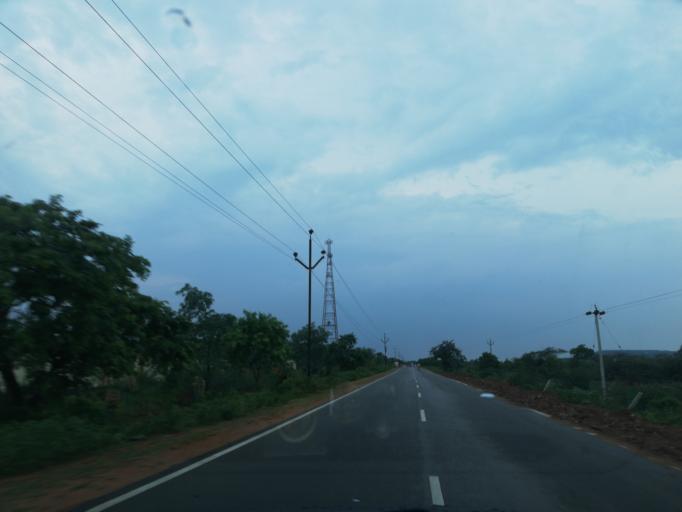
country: IN
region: Andhra Pradesh
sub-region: Guntur
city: Macherla
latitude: 16.6218
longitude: 79.2938
